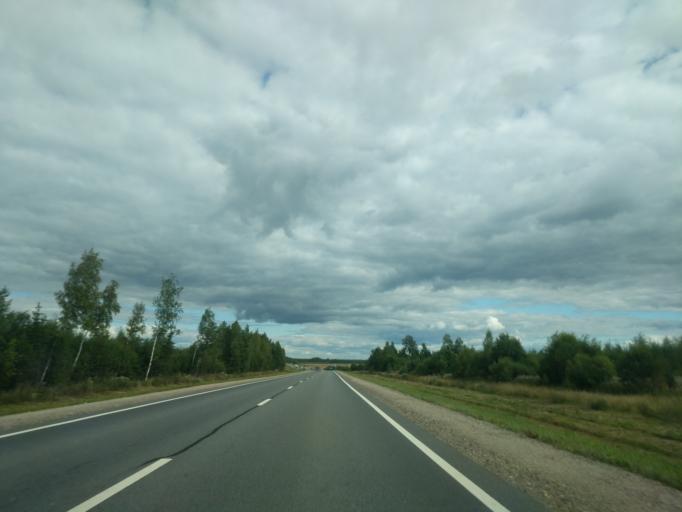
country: RU
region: Kostroma
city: Sudislavl'
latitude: 57.8184
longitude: 41.9363
